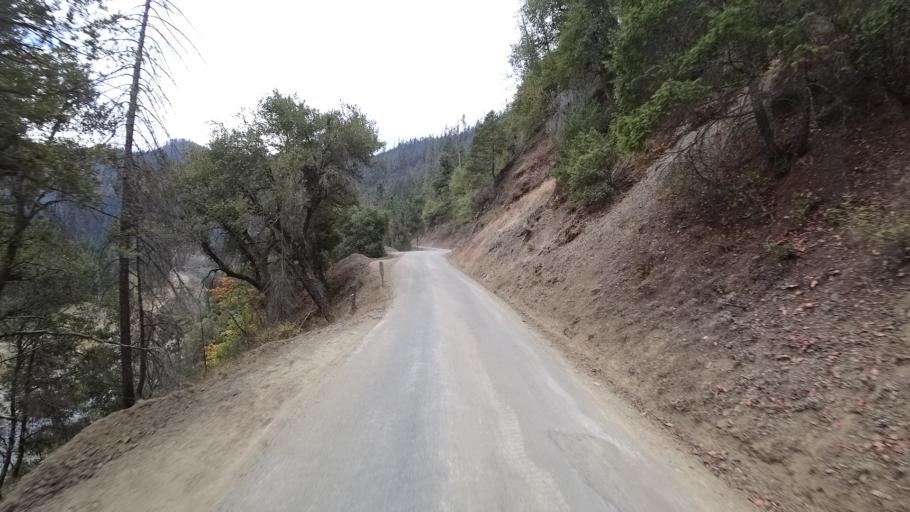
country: US
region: California
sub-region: Siskiyou County
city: Happy Camp
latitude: 41.7744
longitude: -123.3484
